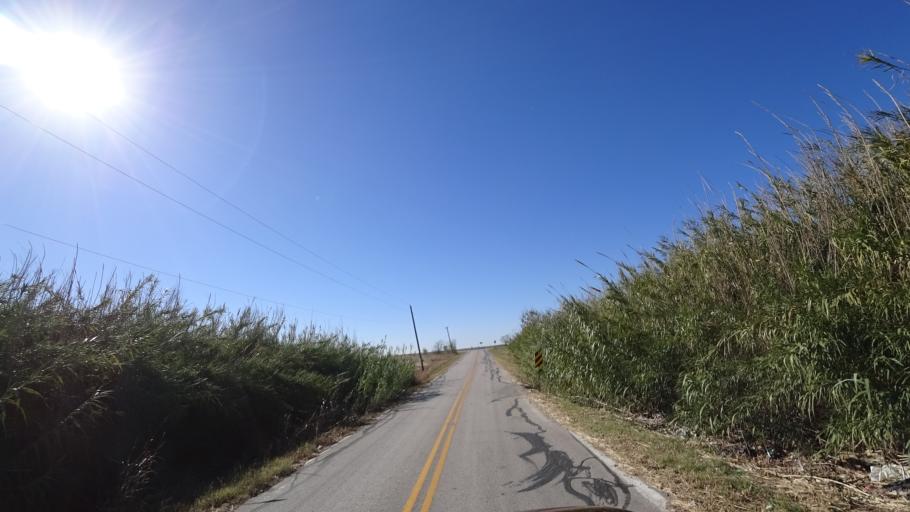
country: US
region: Texas
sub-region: Travis County
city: Garfield
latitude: 30.0996
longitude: -97.6348
